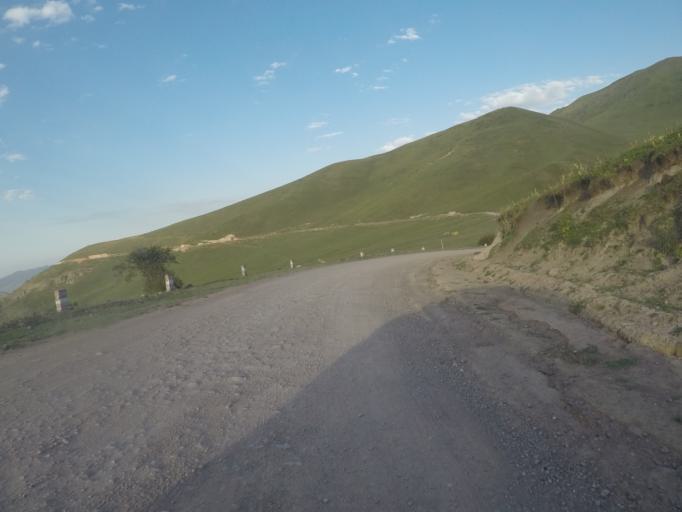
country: KG
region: Chuy
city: Bishkek
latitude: 42.6405
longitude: 74.6365
